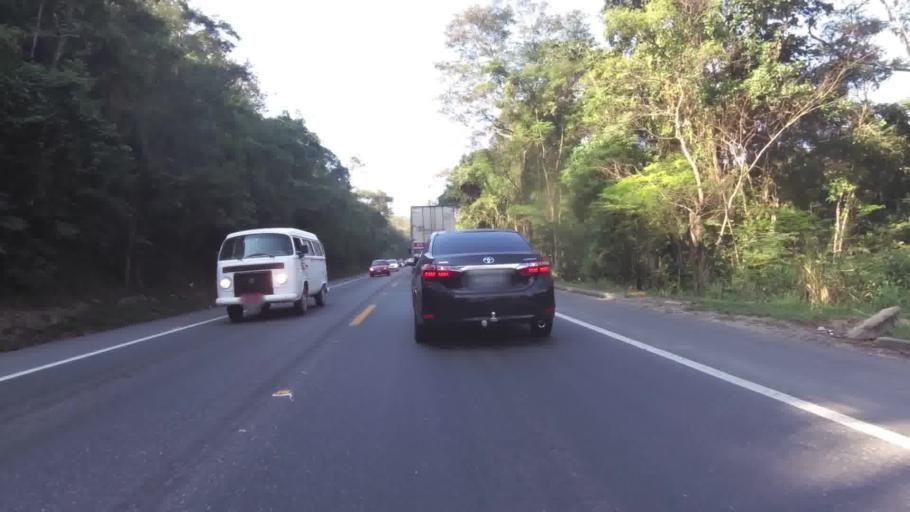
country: BR
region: Espirito Santo
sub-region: Alfredo Chaves
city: Alfredo Chaves
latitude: -20.7126
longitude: -40.7249
